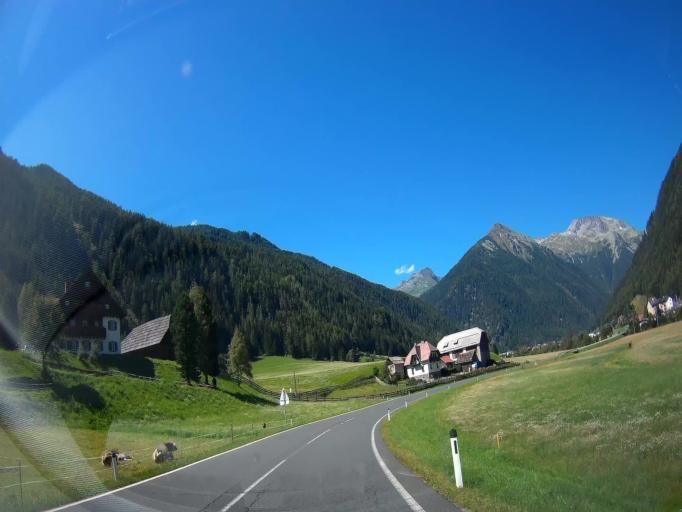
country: AT
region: Carinthia
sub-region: Politischer Bezirk Spittal an der Drau
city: Obervellach
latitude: 46.9737
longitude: 13.1773
